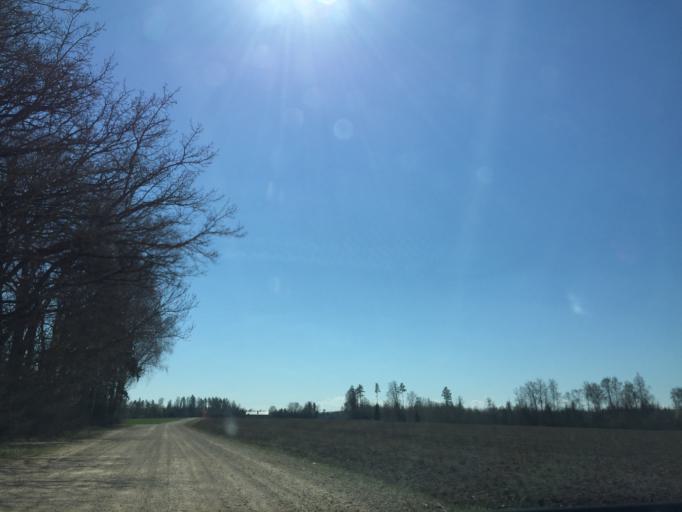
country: EE
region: Viljandimaa
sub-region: Viiratsi vald
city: Viiratsi
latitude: 58.3556
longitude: 25.7219
